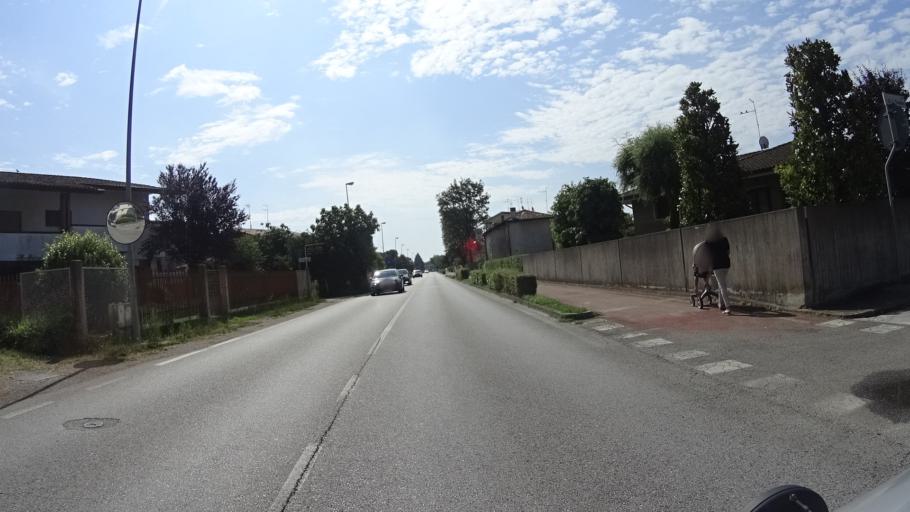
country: IT
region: Friuli Venezia Giulia
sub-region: Provincia di Udine
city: Latisana
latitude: 45.7746
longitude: 13.0127
